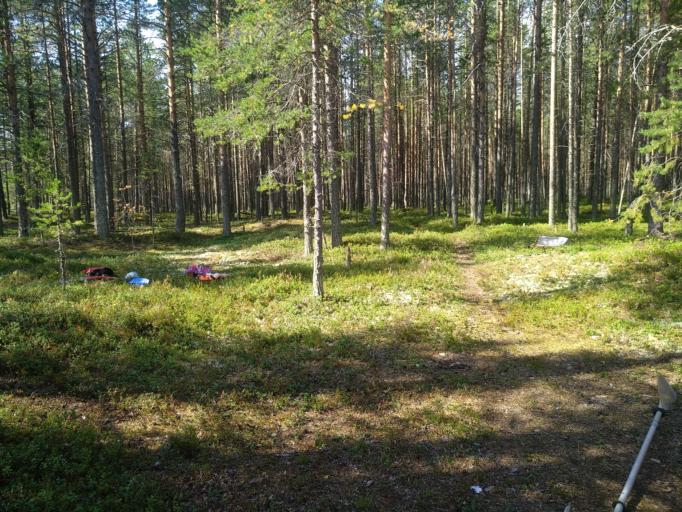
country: RU
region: Republic of Karelia
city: Kostomuksha
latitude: 64.9778
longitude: 30.7354
